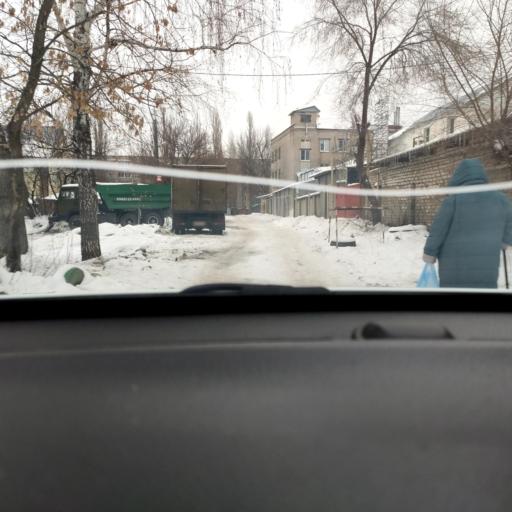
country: RU
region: Voronezj
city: Somovo
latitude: 51.7426
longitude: 39.3581
